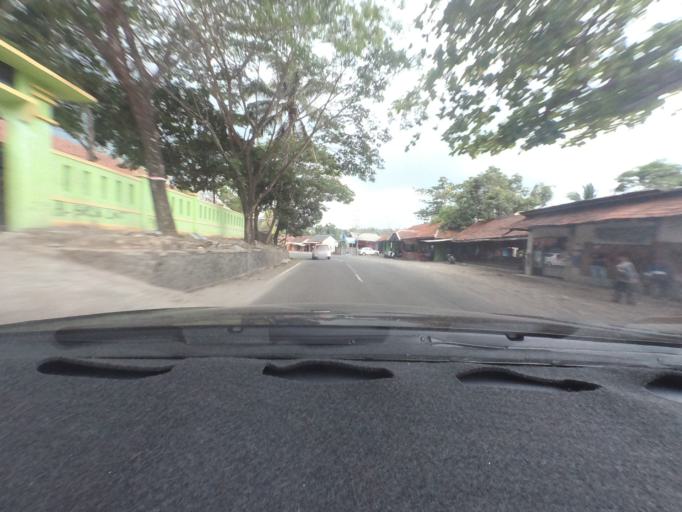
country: ID
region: West Java
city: Sindangsari
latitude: -6.9934
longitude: 106.6692
